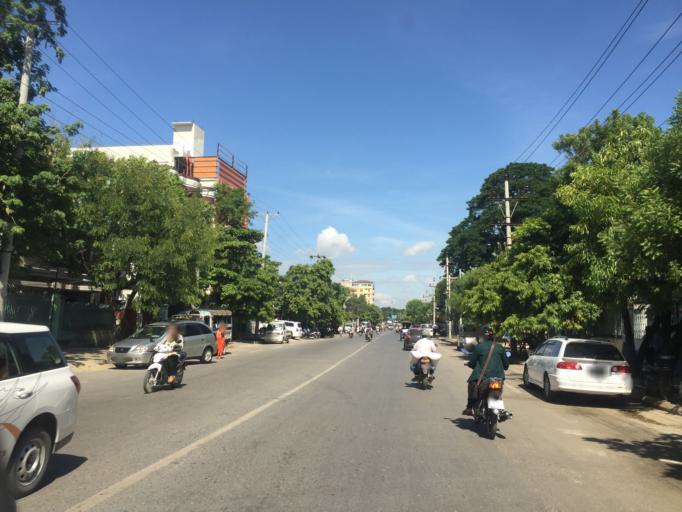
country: MM
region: Mandalay
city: Mandalay
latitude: 21.9840
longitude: 96.0674
